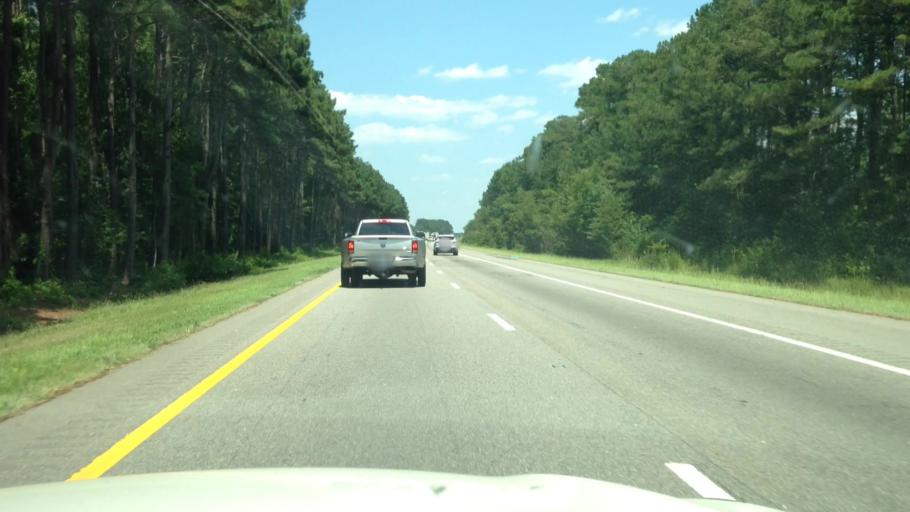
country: US
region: North Carolina
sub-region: Robeson County
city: Fairmont
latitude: 34.5825
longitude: -79.1394
